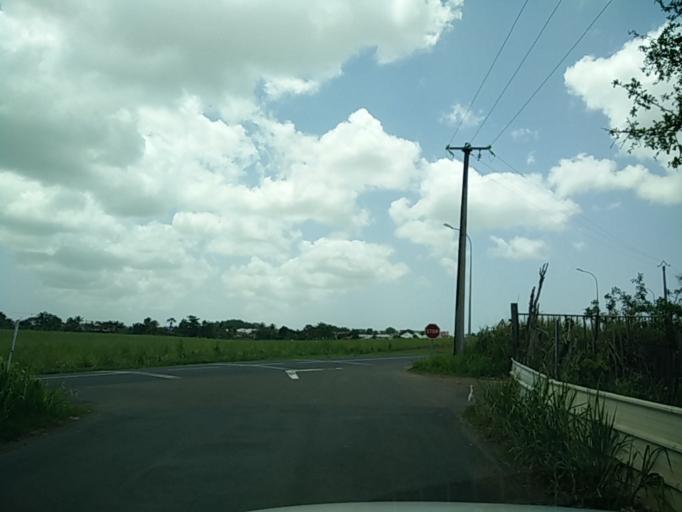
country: GP
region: Guadeloupe
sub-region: Guadeloupe
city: Les Abymes
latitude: 16.2800
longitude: -61.5110
